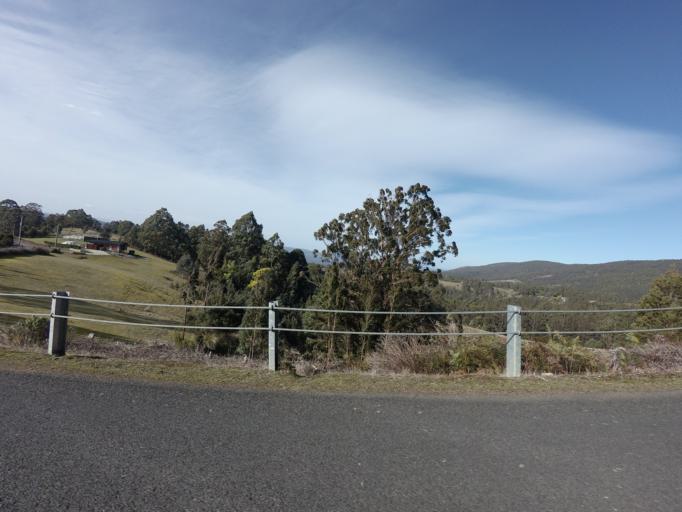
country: AU
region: Tasmania
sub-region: Kingborough
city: Kettering
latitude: -43.1680
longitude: 147.2070
